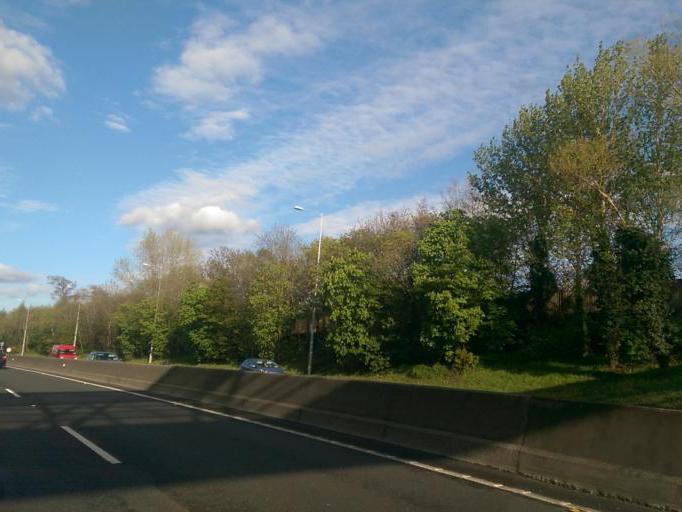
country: IE
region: Leinster
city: Lucan
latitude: 53.3512
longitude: -6.4414
